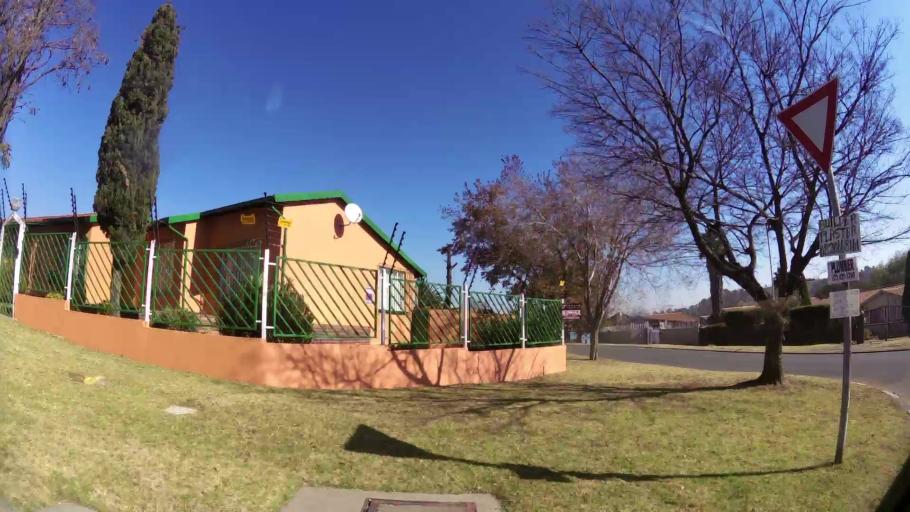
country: ZA
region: Gauteng
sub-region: City of Johannesburg Metropolitan Municipality
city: Johannesburg
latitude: -26.2385
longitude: 28.1016
